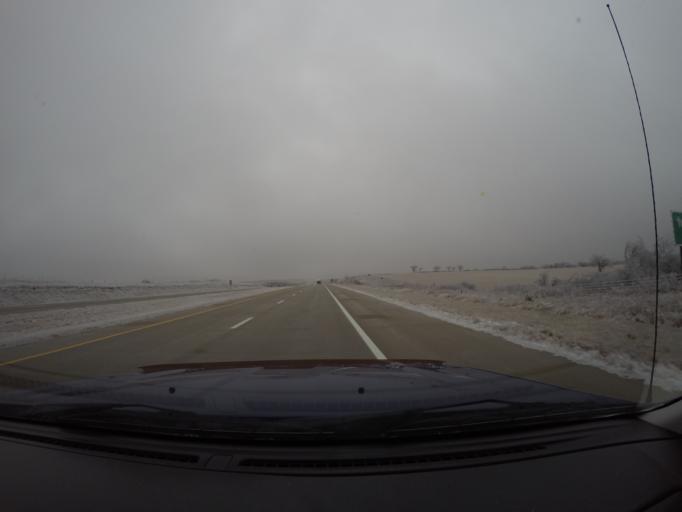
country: US
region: Kansas
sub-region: Wabaunsee County
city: Alma
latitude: 39.0657
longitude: -96.3689
